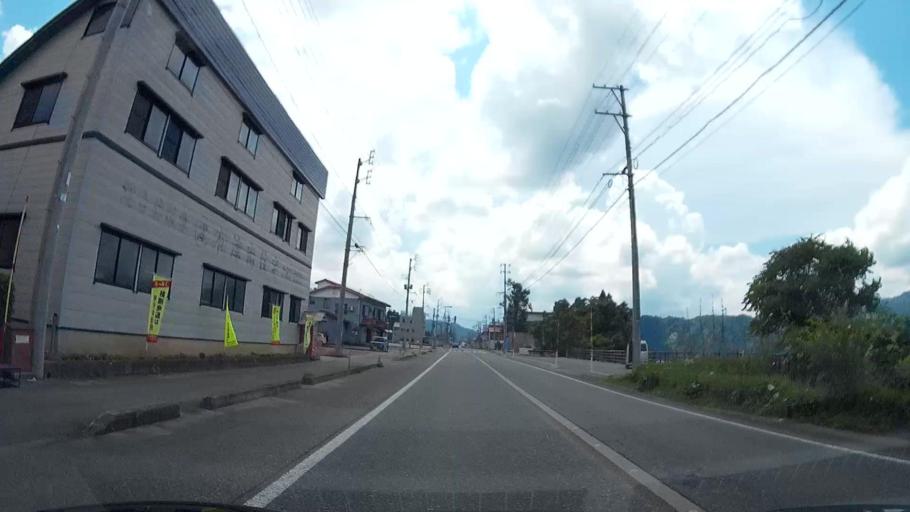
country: JP
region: Niigata
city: Tokamachi
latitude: 37.0244
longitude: 138.6614
